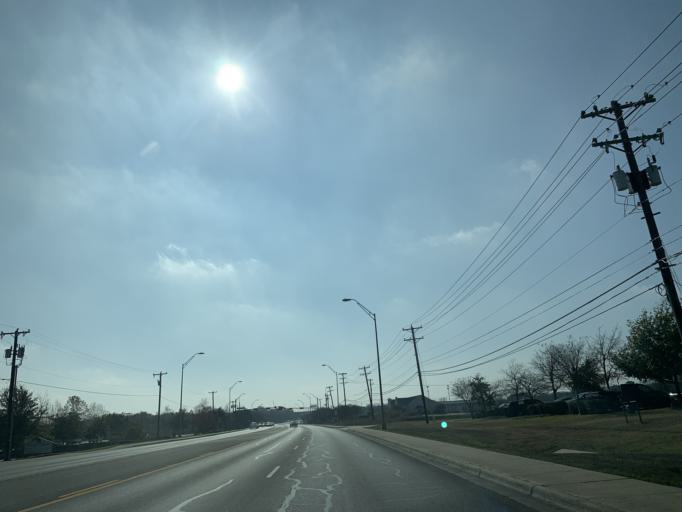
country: US
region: Texas
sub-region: Williamson County
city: Round Rock
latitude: 30.5338
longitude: -97.6522
